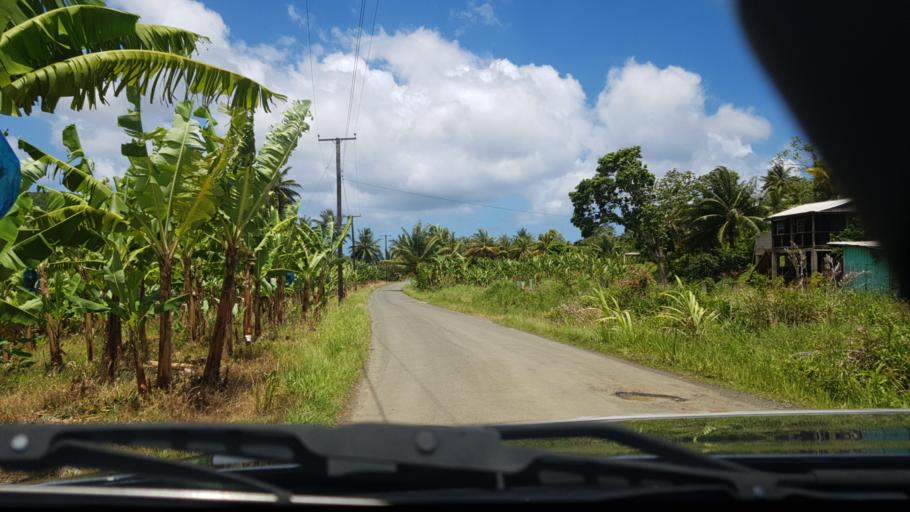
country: LC
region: Anse-la-Raye
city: Anse La Raye
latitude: 13.9474
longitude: -60.9897
